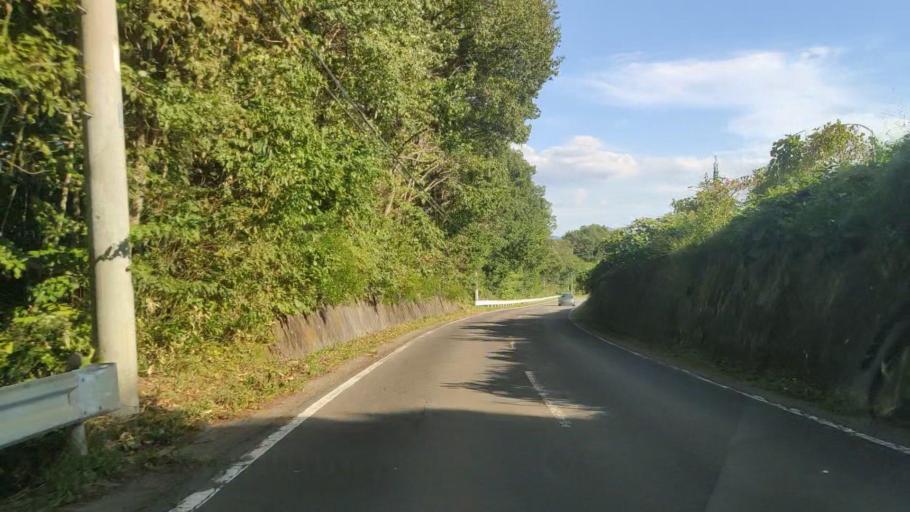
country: JP
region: Nagano
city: Suzaka
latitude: 36.5633
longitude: 138.5558
